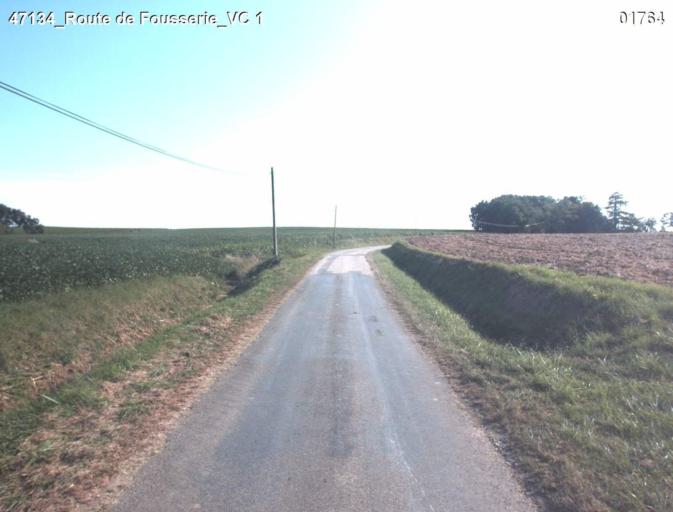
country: FR
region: Aquitaine
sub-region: Departement du Lot-et-Garonne
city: Mezin
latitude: 44.0315
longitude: 0.2874
